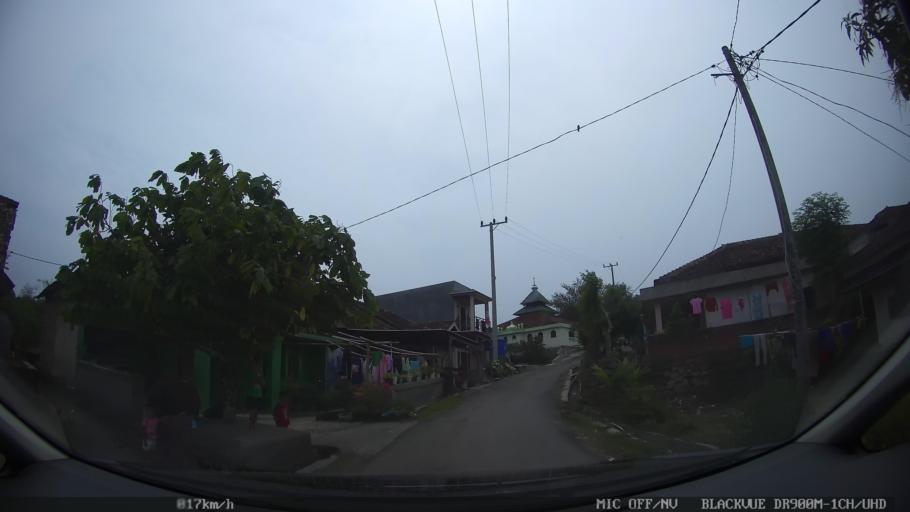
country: ID
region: Lampung
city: Bandarlampung
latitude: -5.4225
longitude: 105.3057
